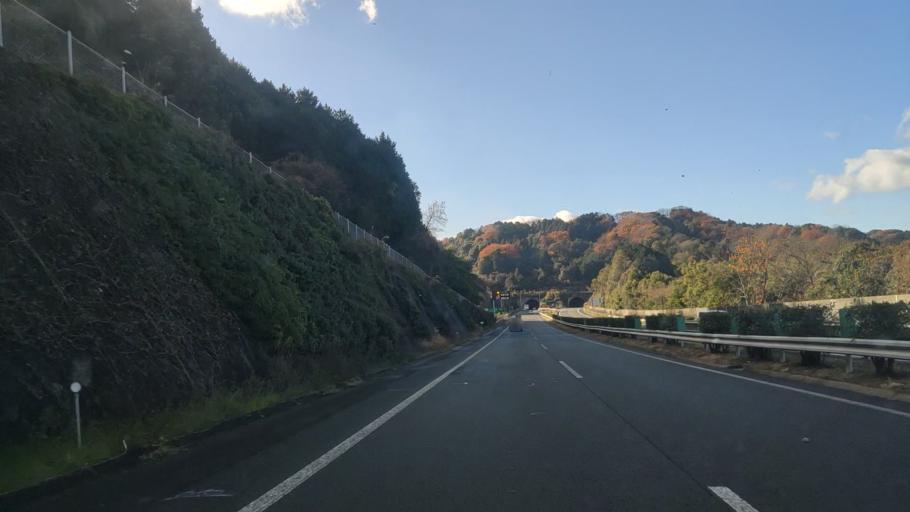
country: JP
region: Ehime
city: Niihama
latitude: 33.9093
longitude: 133.2609
